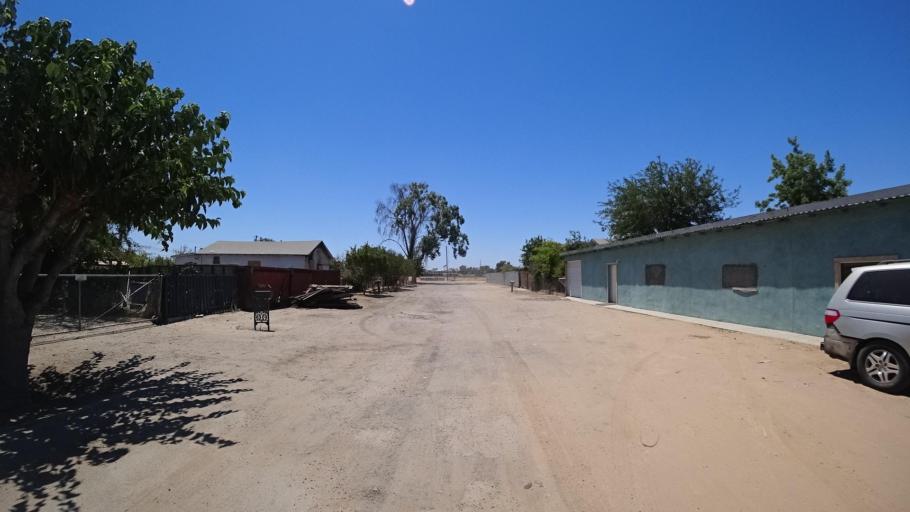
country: US
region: California
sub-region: Fresno County
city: Fresno
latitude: 36.7168
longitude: -119.7750
